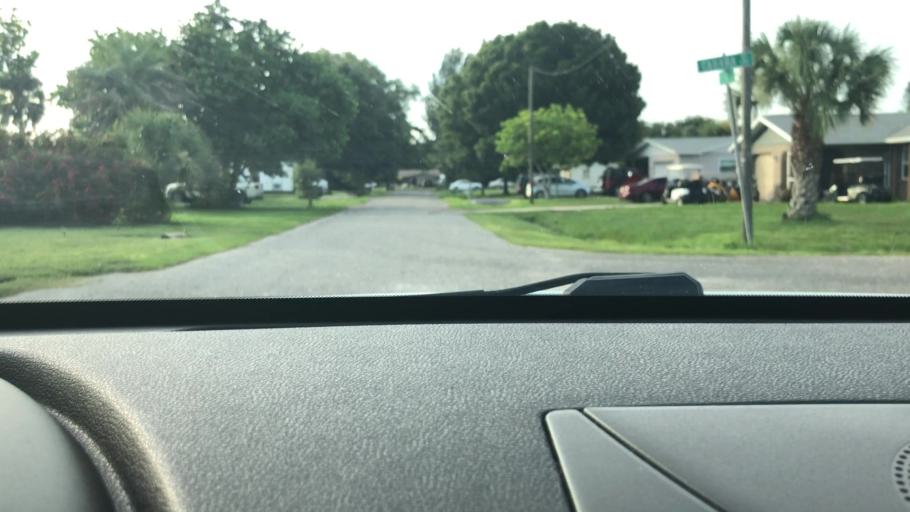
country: US
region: Florida
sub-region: Sarasota County
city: South Venice
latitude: 27.0434
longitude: -82.4129
